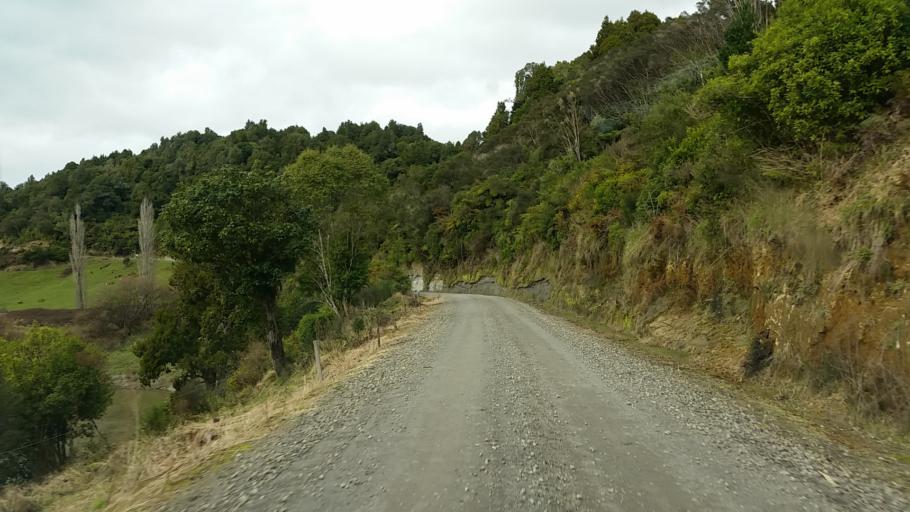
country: NZ
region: Taranaki
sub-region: New Plymouth District
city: Waitara
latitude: -39.1588
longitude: 174.5277
